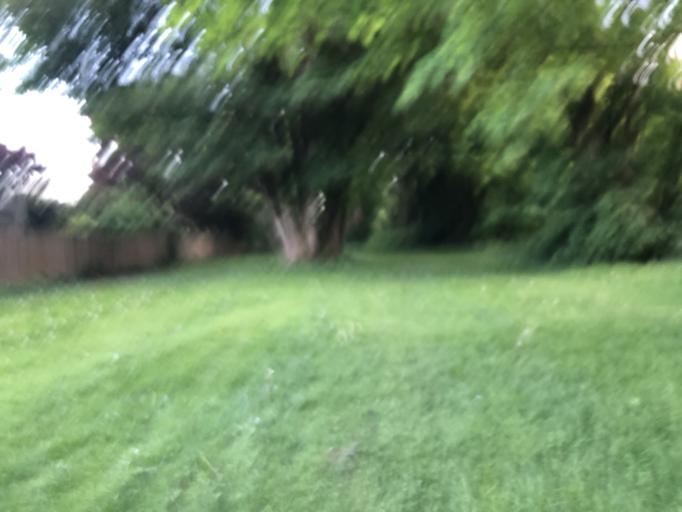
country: CA
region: British Columbia
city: Richmond
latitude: 49.1345
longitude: -123.1253
